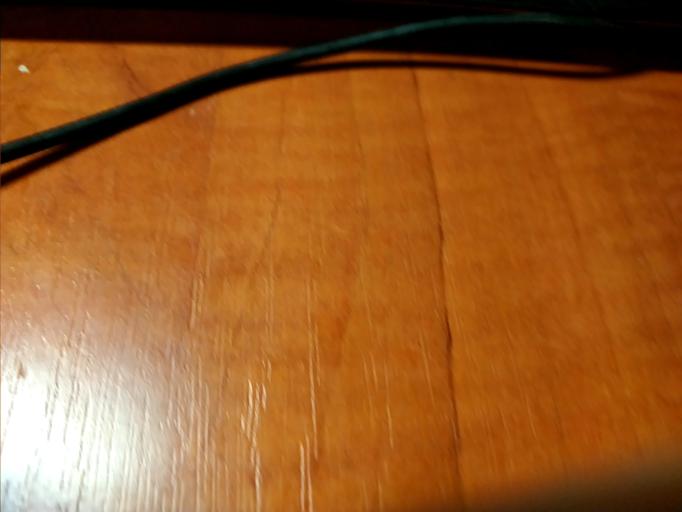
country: RU
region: Tverskaya
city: Rameshki
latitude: 57.4399
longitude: 36.0434
